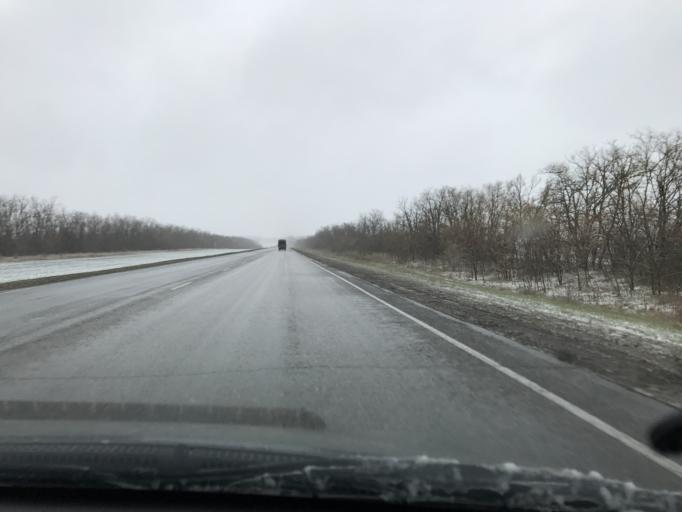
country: RU
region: Rostov
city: Mechetinskaya
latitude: 46.7244
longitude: 40.4841
